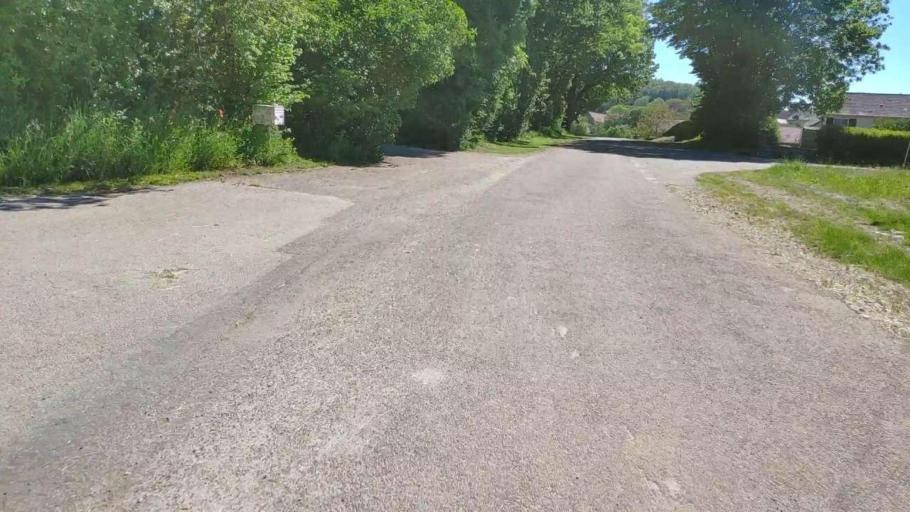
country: FR
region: Franche-Comte
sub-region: Departement du Jura
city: Clairvaux-les-Lacs
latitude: 46.6994
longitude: 5.7226
